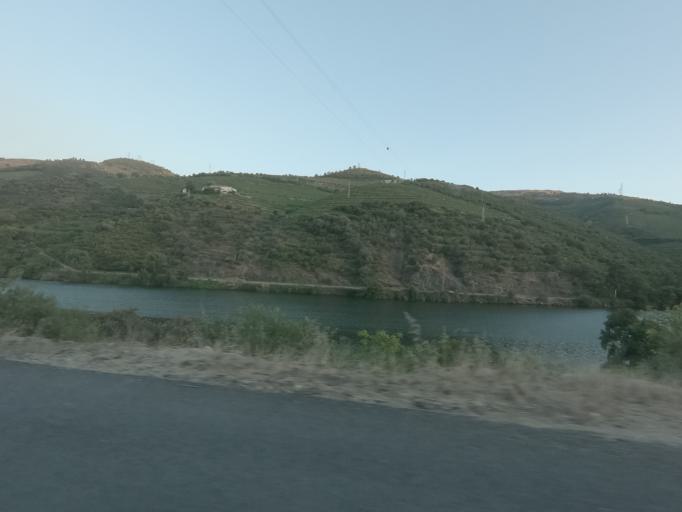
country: PT
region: Viseu
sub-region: Armamar
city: Armamar
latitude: 41.1464
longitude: -7.7303
